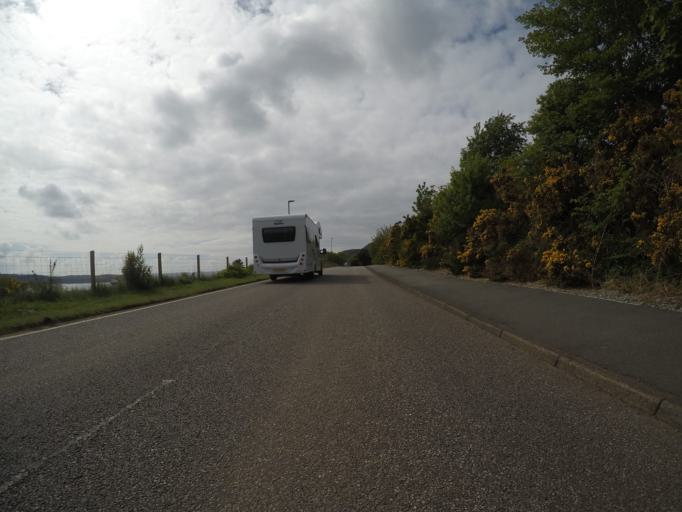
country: GB
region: Scotland
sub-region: Highland
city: Portree
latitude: 57.5913
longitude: -6.3631
